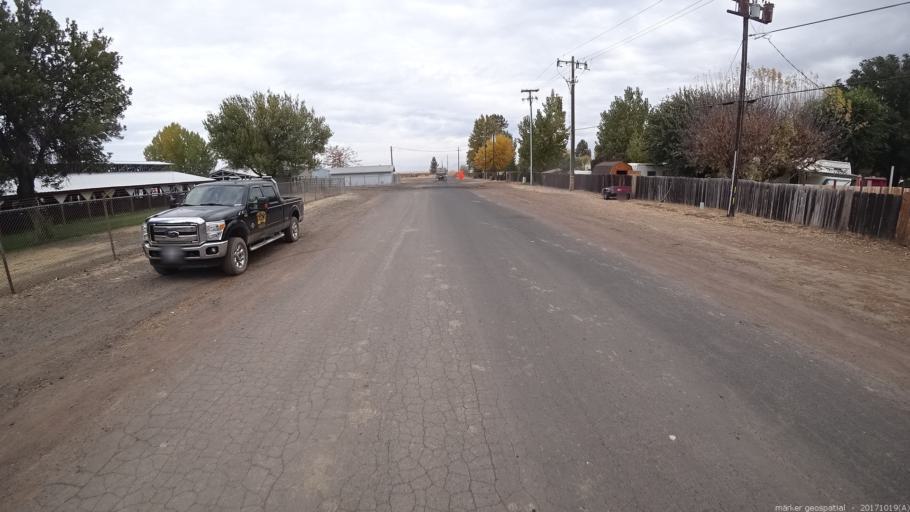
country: US
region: California
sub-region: Shasta County
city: Burney
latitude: 41.0517
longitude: -121.3986
